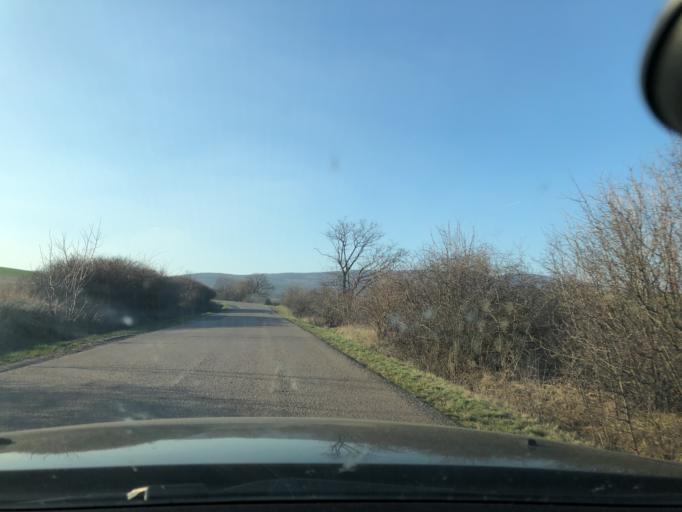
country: HU
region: Nograd
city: Paszto
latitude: 47.9066
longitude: 19.6658
